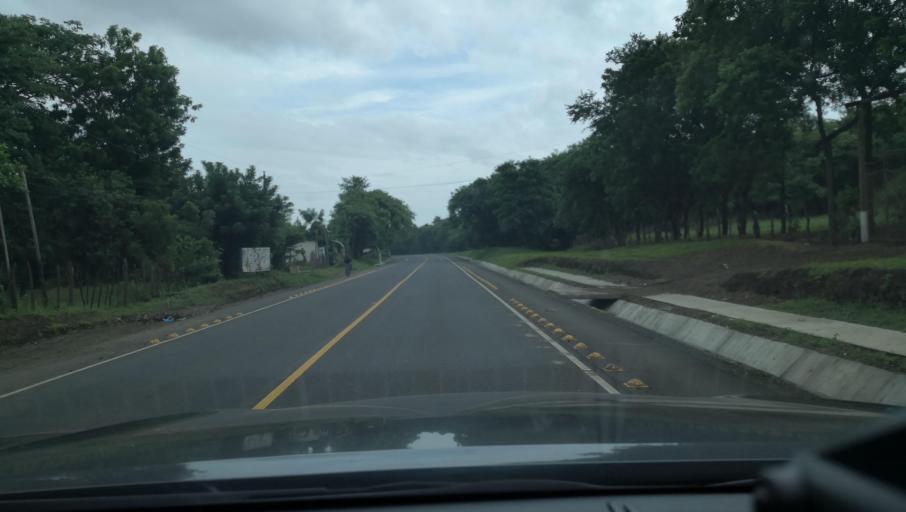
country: NI
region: Masaya
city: Nindiri
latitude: 12.0723
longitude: -86.1384
